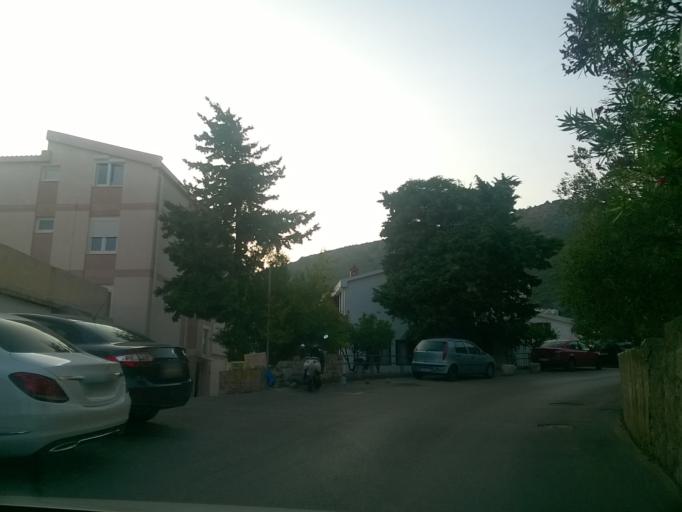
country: ME
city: Petrovac na Moru
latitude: 42.2063
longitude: 18.9457
